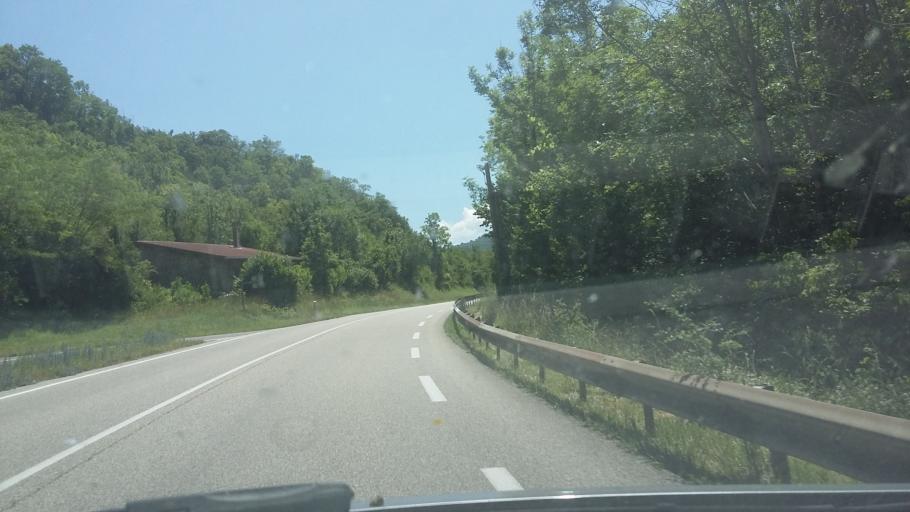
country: FR
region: Rhone-Alpes
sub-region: Departement de l'Ain
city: Tenay
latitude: 45.9456
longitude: 5.4800
